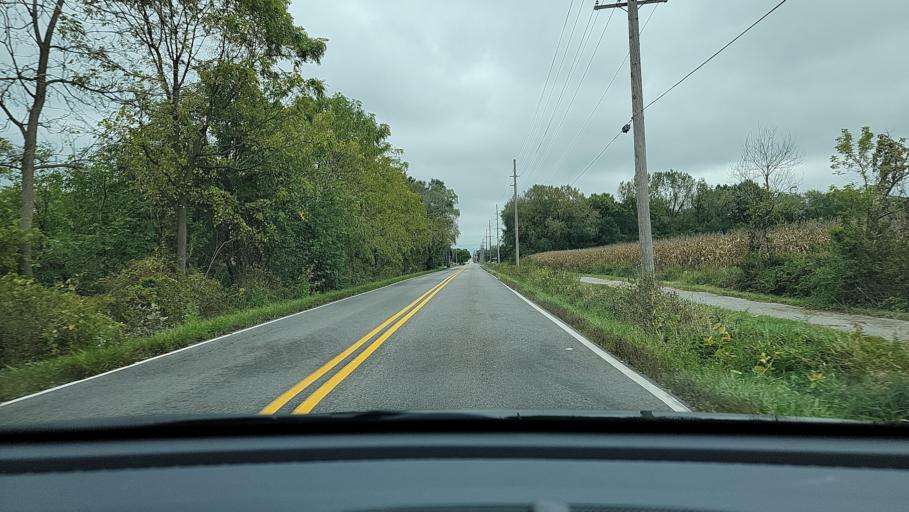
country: US
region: Indiana
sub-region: Porter County
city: Portage
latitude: 41.5578
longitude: -87.1898
